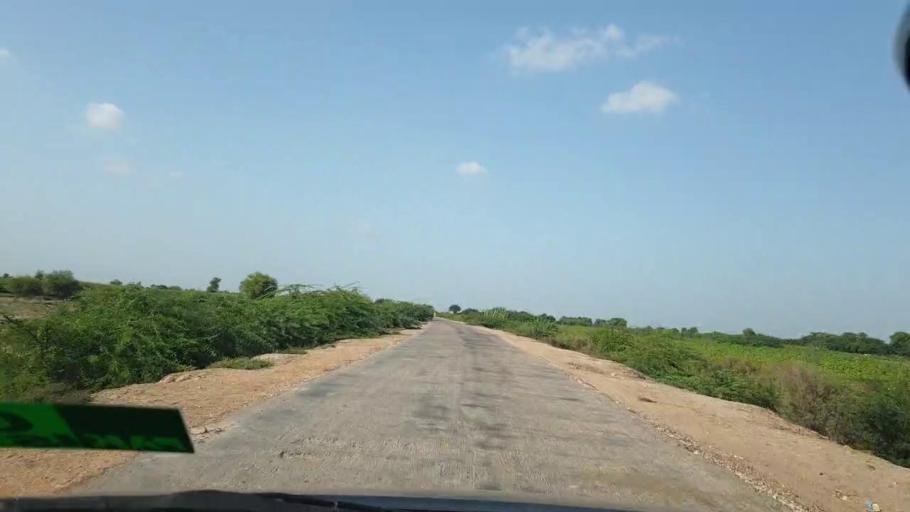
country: PK
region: Sindh
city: Tando Bago
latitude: 24.7163
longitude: 69.1937
